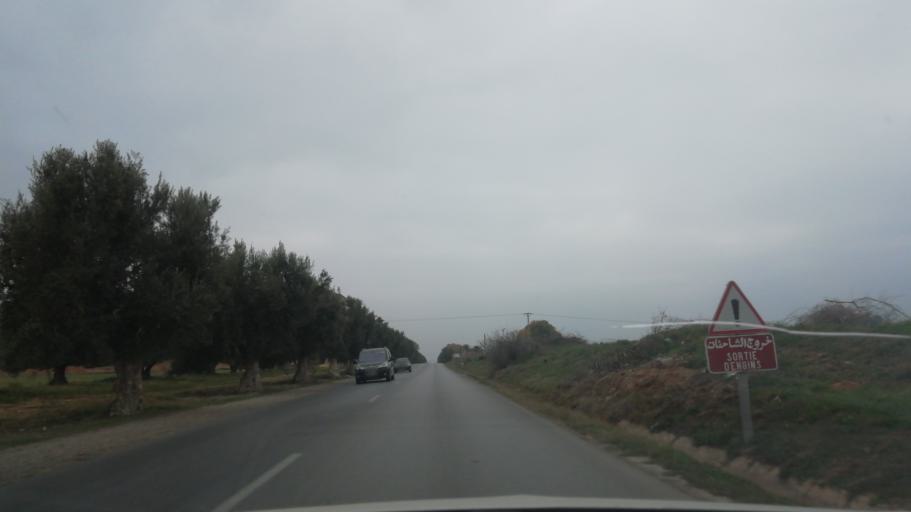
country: DZ
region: Sidi Bel Abbes
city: Sfizef
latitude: 35.2290
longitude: -0.2631
